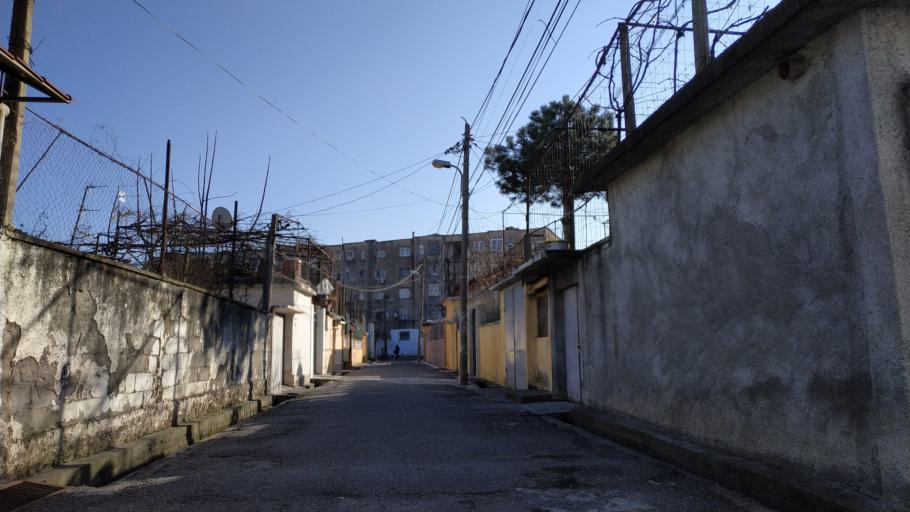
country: AL
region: Shkoder
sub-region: Rrethi i Shkodres
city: Shkoder
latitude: 42.0626
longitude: 19.5230
